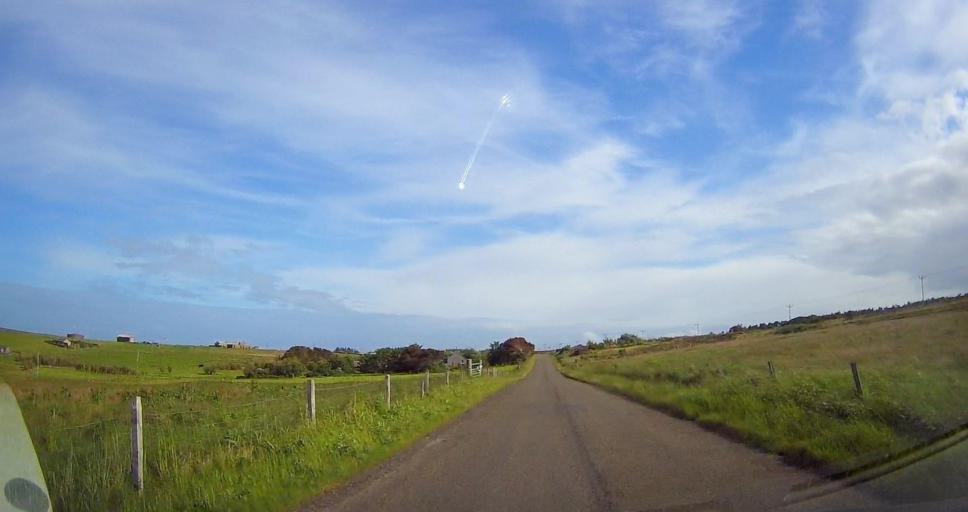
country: GB
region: Scotland
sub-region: Orkney Islands
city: Stromness
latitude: 58.8375
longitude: -3.2155
